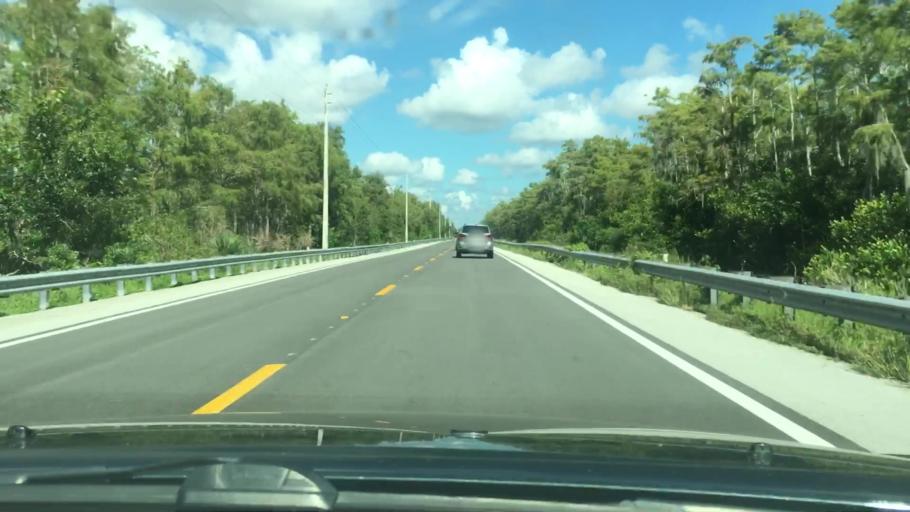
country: US
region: Florida
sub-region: Miami-Dade County
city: Kendall West
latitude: 25.7983
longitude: -80.8657
